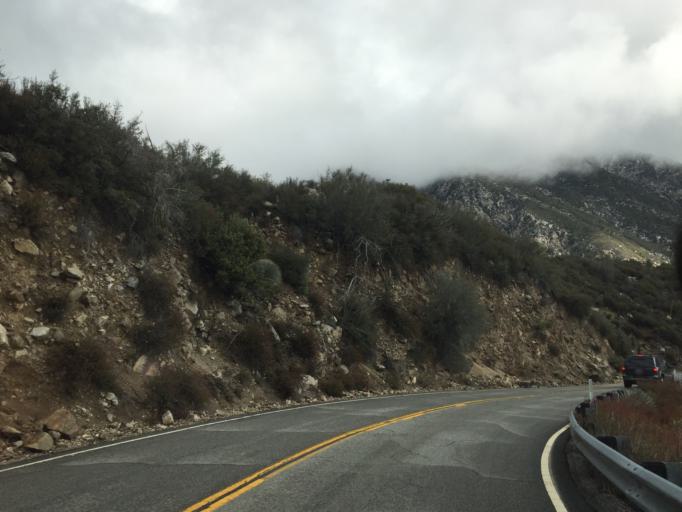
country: US
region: California
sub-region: Los Angeles County
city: Glendora
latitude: 34.3030
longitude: -117.8453
